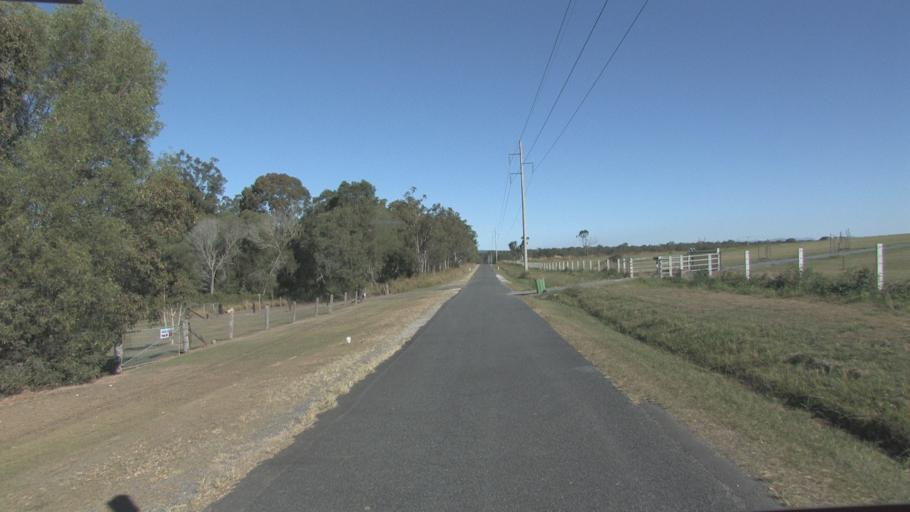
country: AU
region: Queensland
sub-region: Logan
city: Chambers Flat
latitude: -27.7713
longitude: 153.0597
